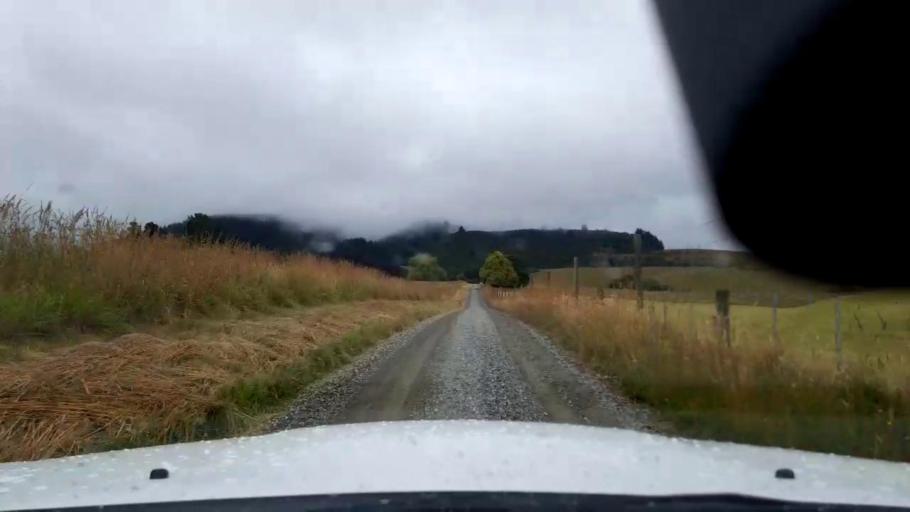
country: NZ
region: Canterbury
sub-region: Timaru District
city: Pleasant Point
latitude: -44.0754
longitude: 171.1463
